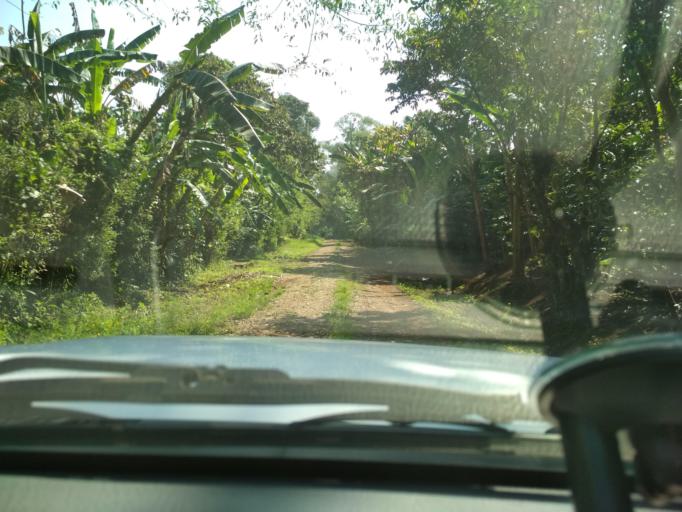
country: MX
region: Veracruz
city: Monte Blanco
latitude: 18.9799
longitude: -97.0107
